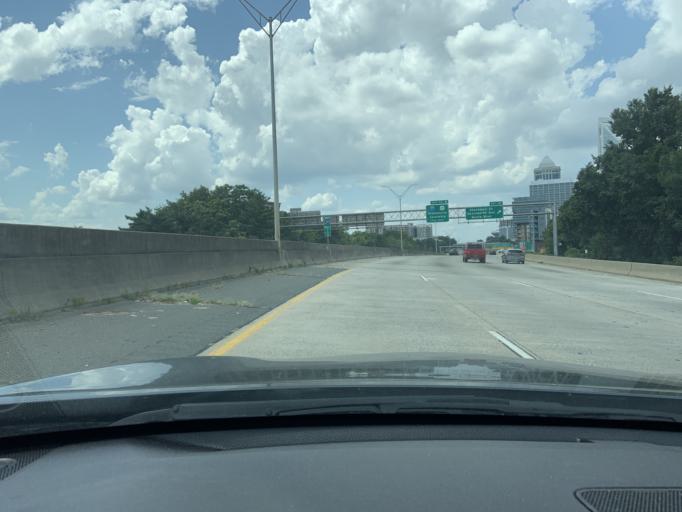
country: US
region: North Carolina
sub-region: Mecklenburg County
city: Charlotte
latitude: 35.2153
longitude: -80.8412
